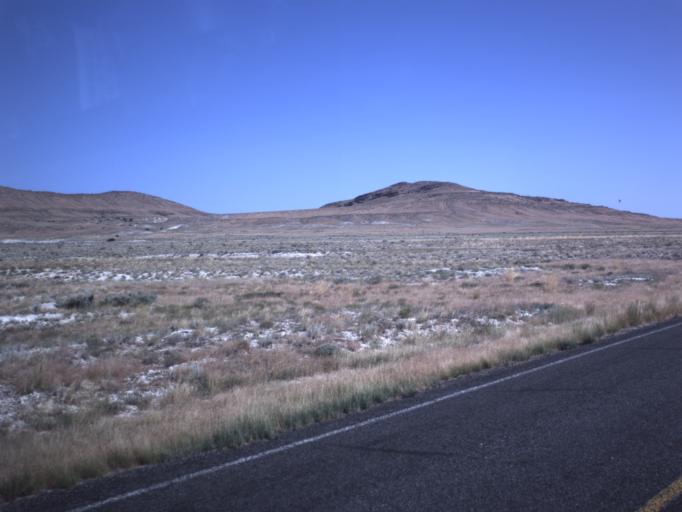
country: US
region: Utah
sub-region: Beaver County
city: Milford
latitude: 38.8613
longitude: -112.8385
